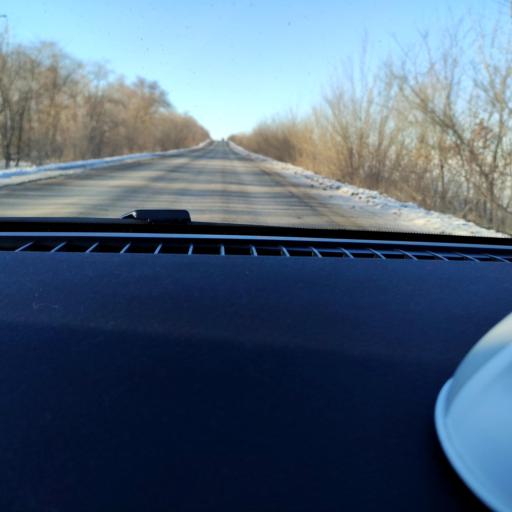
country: RU
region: Samara
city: Spiridonovka
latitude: 53.1445
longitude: 50.5384
